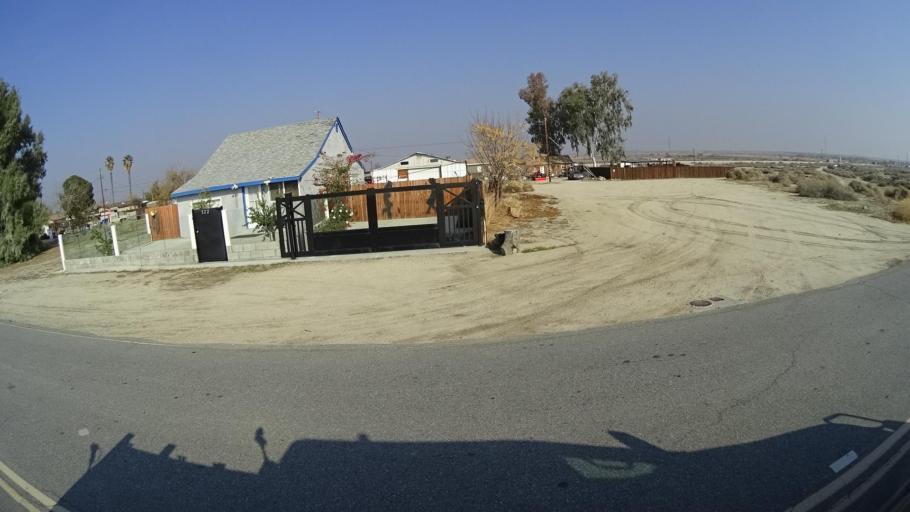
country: US
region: California
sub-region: Kern County
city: Buttonwillow
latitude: 35.2970
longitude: -119.3504
